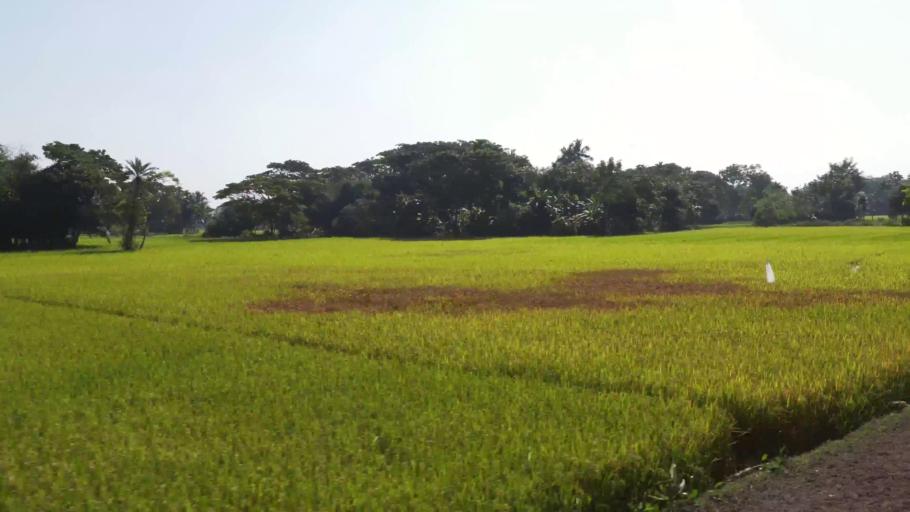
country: BD
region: Dhaka
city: Gafargaon
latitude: 24.5080
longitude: 90.5161
